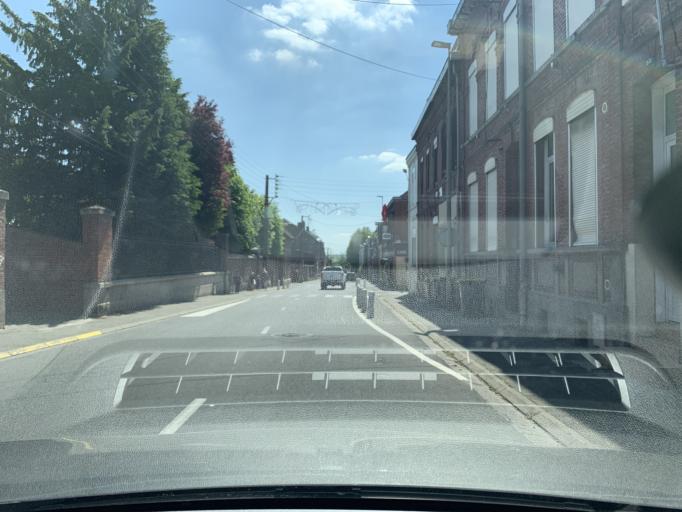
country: FR
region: Nord-Pas-de-Calais
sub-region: Departement du Nord
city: Caudry
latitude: 50.1141
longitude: 3.4092
